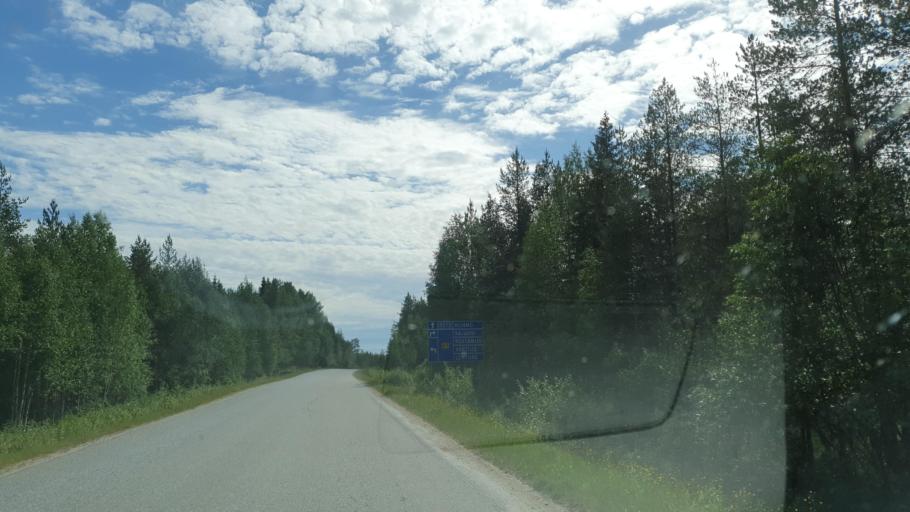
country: FI
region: Kainuu
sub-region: Kehys-Kainuu
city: Kuhmo
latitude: 64.4619
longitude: 29.5354
